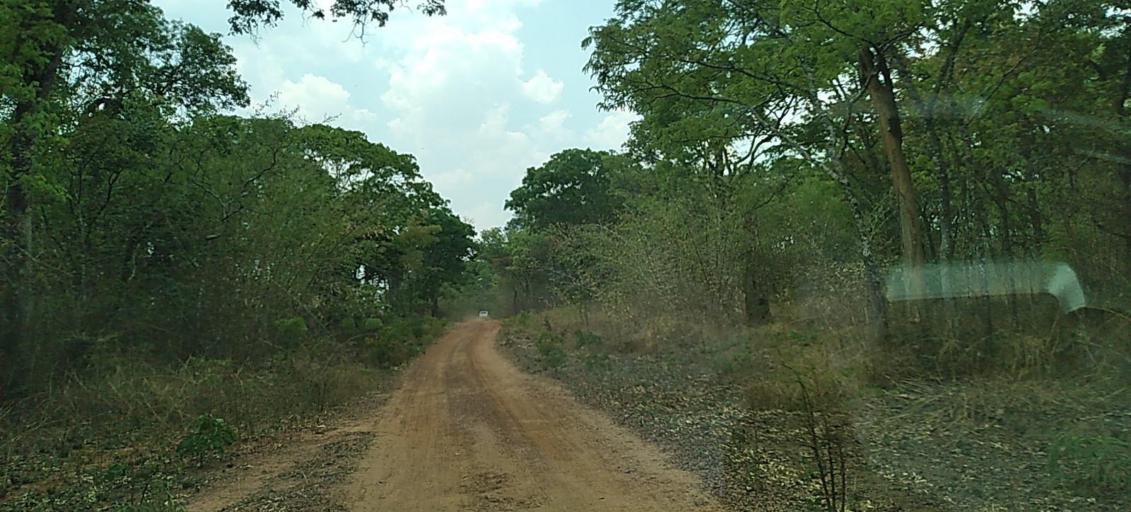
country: ZM
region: Copperbelt
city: Chingola
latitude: -12.7980
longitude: 27.6438
